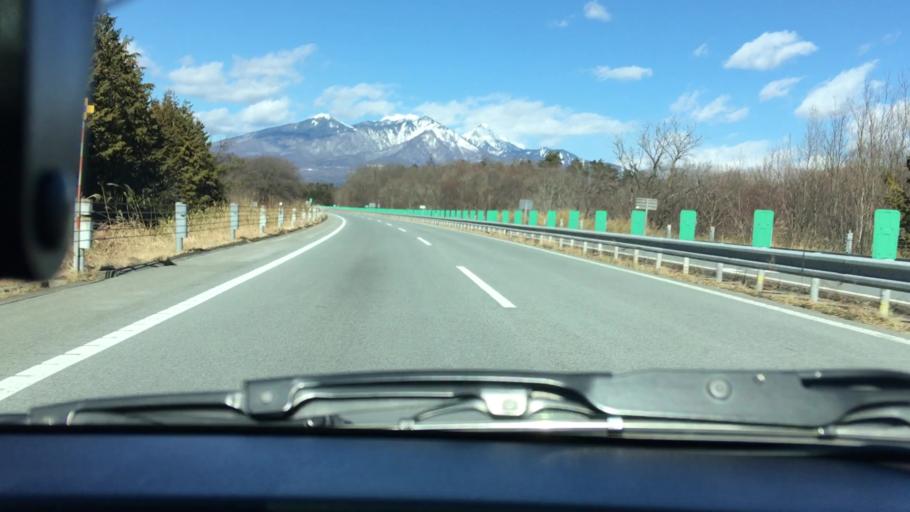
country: JP
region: Yamanashi
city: Nirasaki
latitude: 35.8090
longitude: 138.3957
